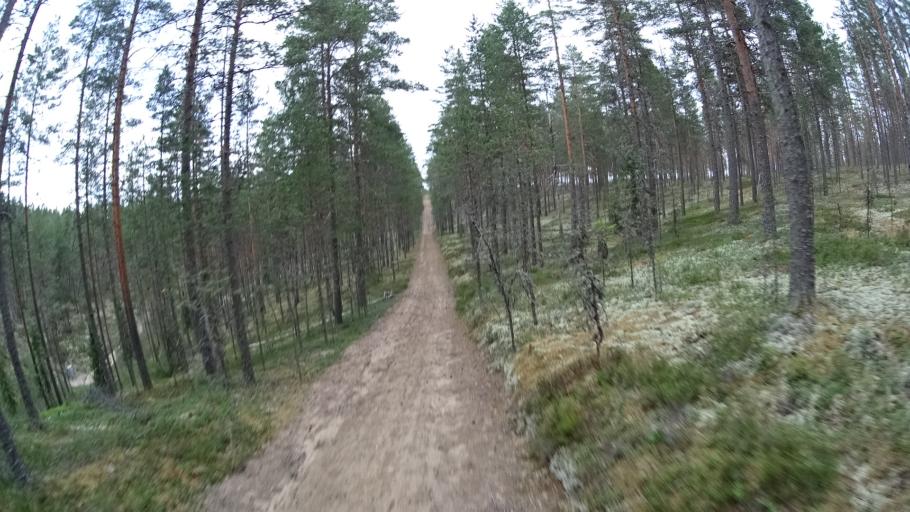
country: FI
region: Satakunta
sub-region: Pohjois-Satakunta
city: Jaemijaervi
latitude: 61.7680
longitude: 22.7900
